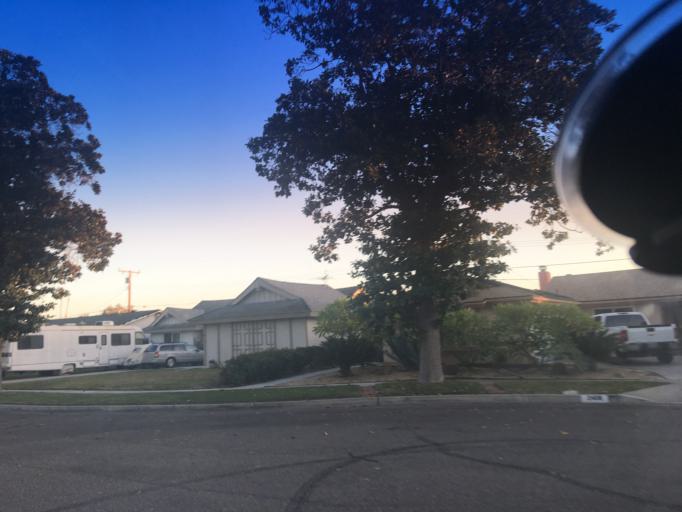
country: US
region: California
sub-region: Orange County
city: Anaheim
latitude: 33.8243
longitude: -117.8822
